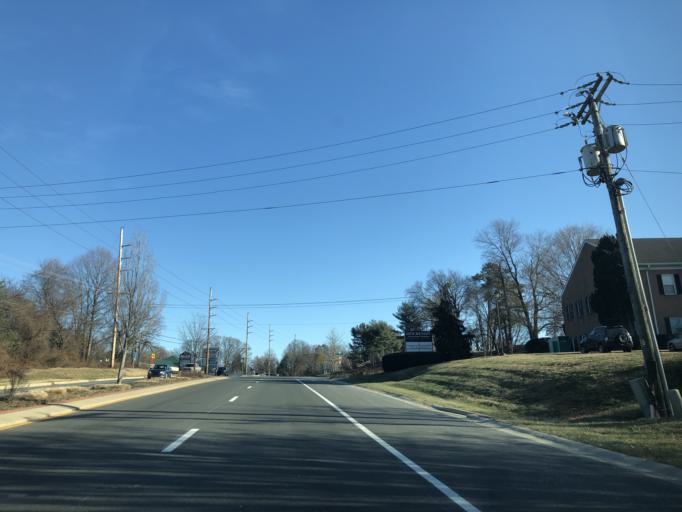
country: US
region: Delaware
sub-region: New Castle County
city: Hockessin
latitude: 39.7864
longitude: -75.6881
